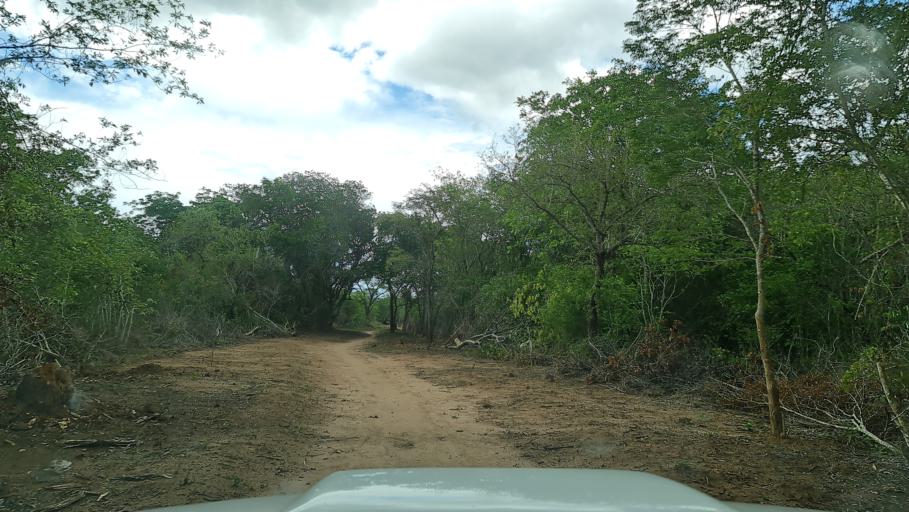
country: MZ
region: Nampula
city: Ilha de Mocambique
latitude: -15.5021
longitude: 40.1843
